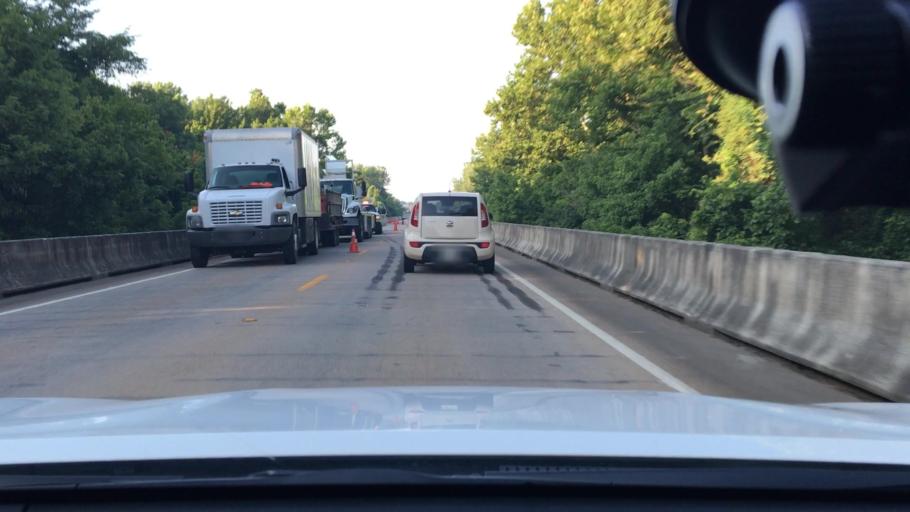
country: US
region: Arkansas
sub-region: Johnson County
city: Clarksville
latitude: 35.4015
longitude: -93.5312
